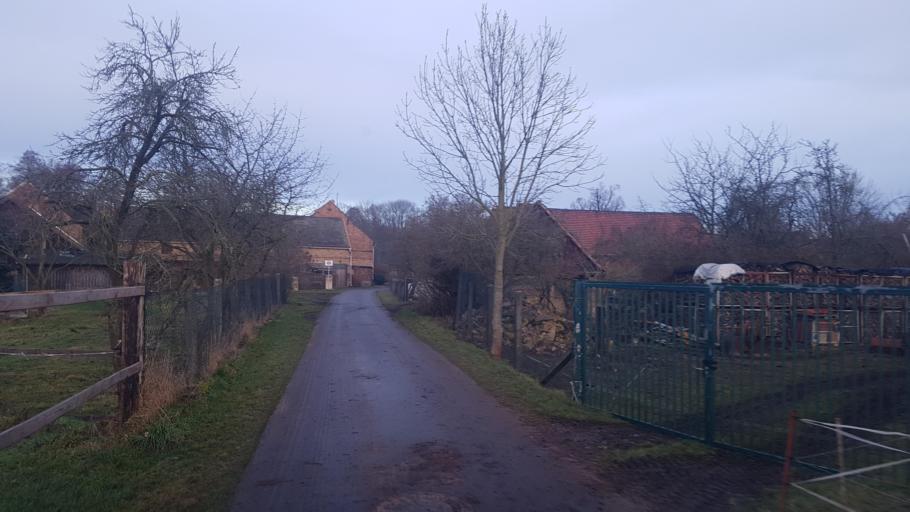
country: DE
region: Brandenburg
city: Drahnsdorf
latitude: 51.9074
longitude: 13.5199
